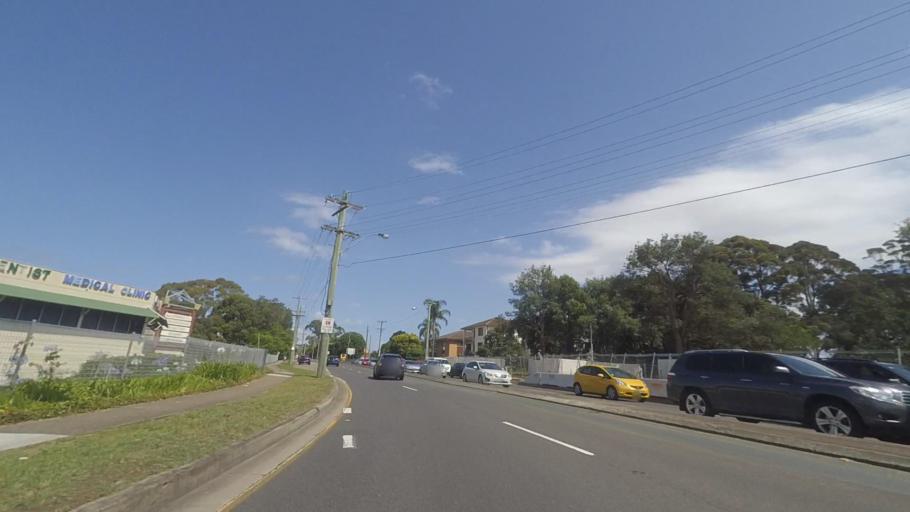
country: AU
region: New South Wales
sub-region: Parramatta
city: Carlingford
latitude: -33.7799
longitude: 151.0527
